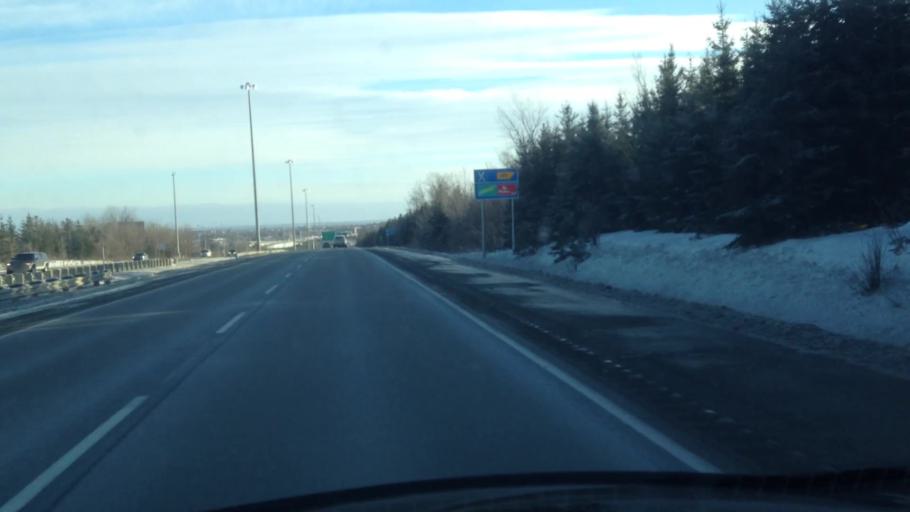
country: CA
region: Quebec
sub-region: Laurentides
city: Saint-Jerome
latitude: 45.8044
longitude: -74.0362
